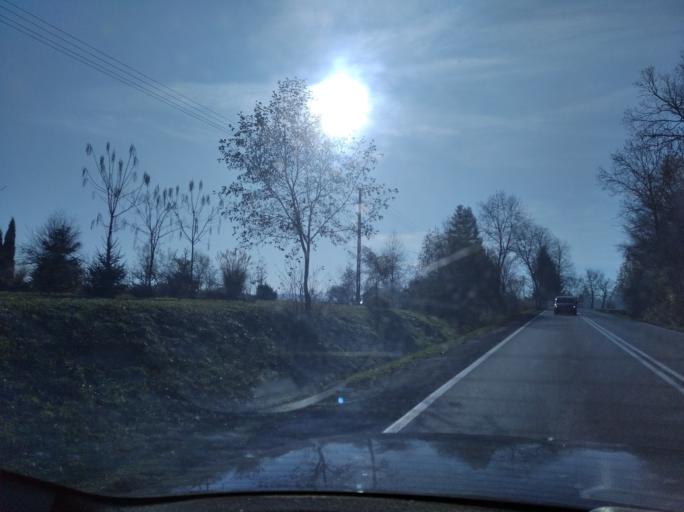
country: PL
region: Subcarpathian Voivodeship
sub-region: Powiat ropczycko-sedziszowski
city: Wielopole Skrzynskie
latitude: 49.9373
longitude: 21.6165
